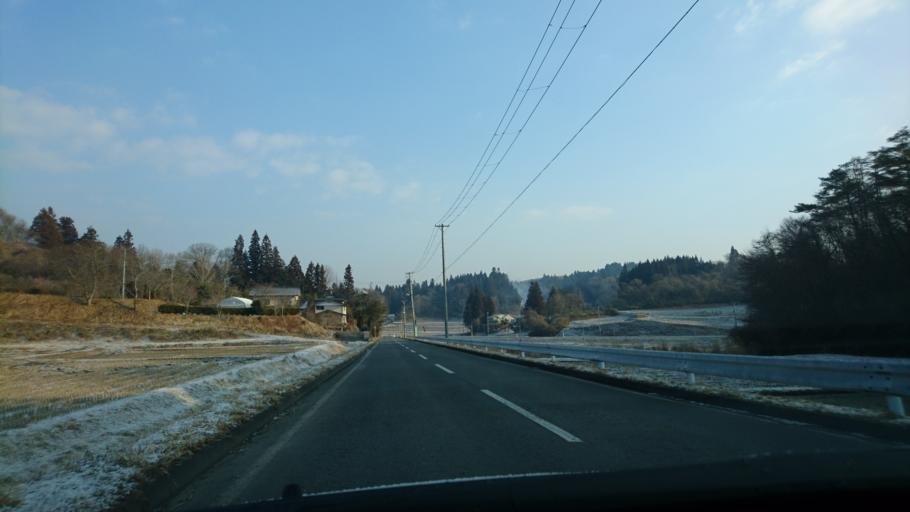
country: JP
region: Iwate
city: Ichinoseki
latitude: 38.9236
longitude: 141.3854
